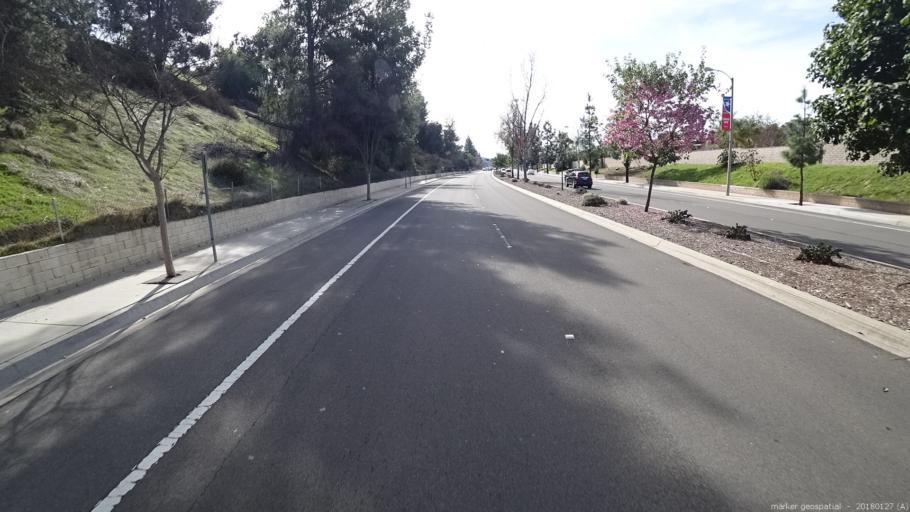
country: US
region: California
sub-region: Los Angeles County
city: Diamond Bar
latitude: 34.0053
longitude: -117.8086
